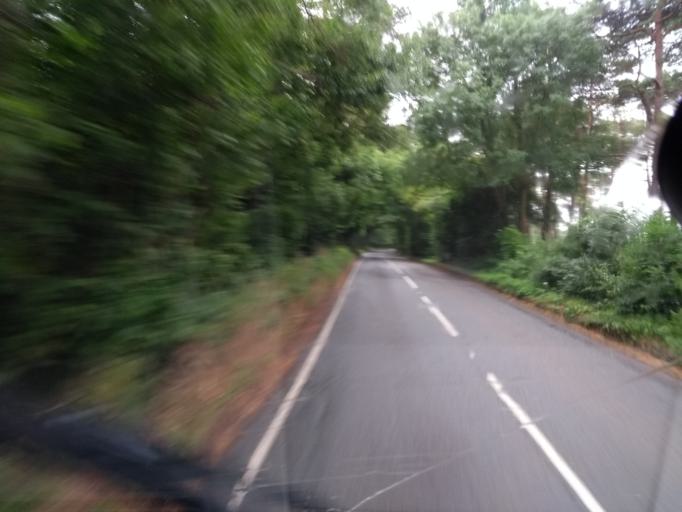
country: GB
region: England
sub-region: Somerset
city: Street
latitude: 51.1059
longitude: -2.7329
